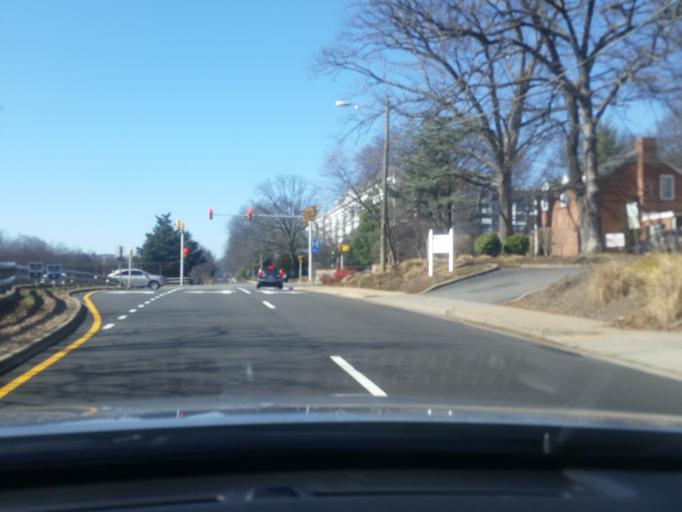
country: US
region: Virginia
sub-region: Arlington County
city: Arlington
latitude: 38.8695
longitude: -77.1061
